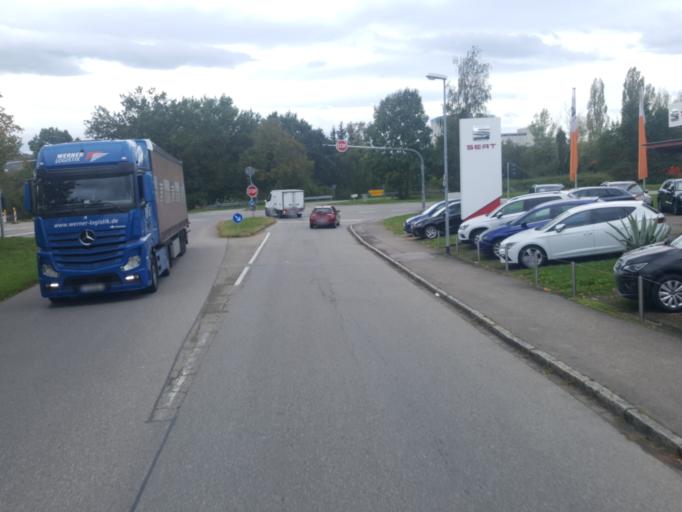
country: CH
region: Aargau
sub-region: Bezirk Rheinfelden
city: Kaiseraugst
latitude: 47.5465
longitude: 7.7387
